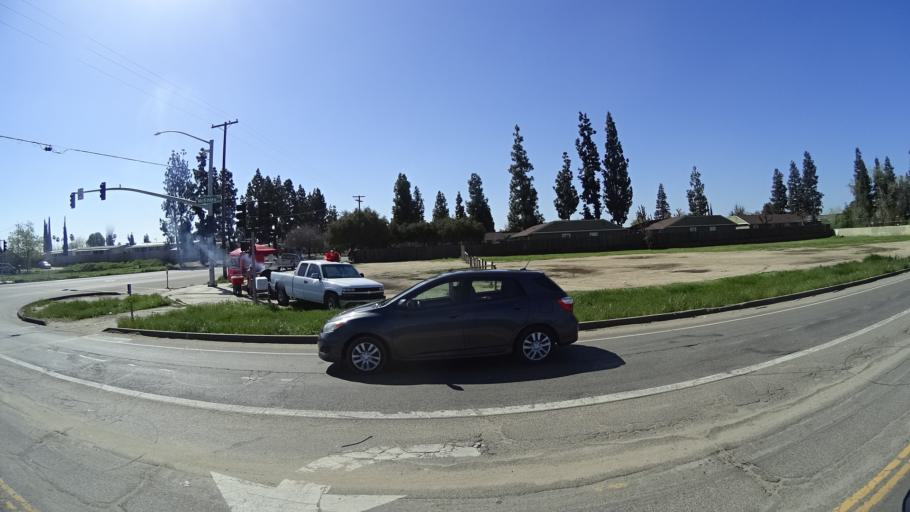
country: US
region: California
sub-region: Fresno County
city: West Park
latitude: 36.7648
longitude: -119.8446
